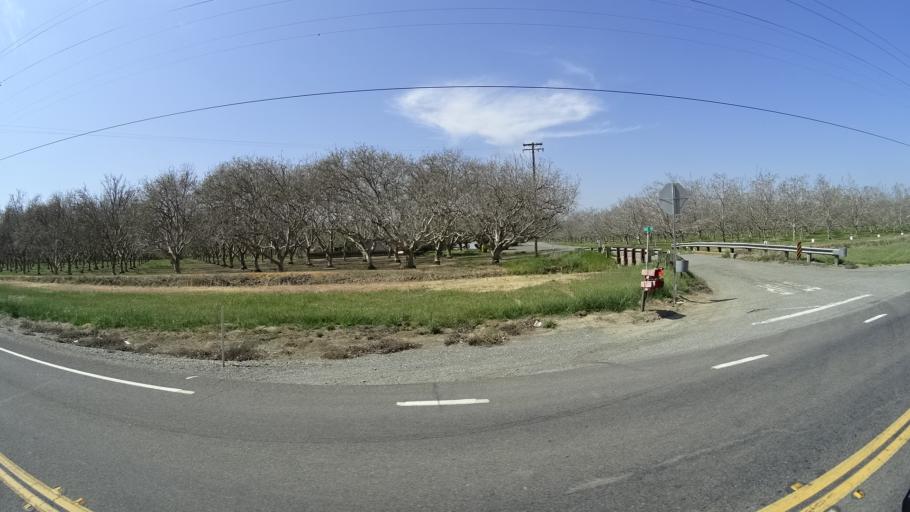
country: US
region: California
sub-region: Glenn County
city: Willows
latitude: 39.4808
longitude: -122.0193
